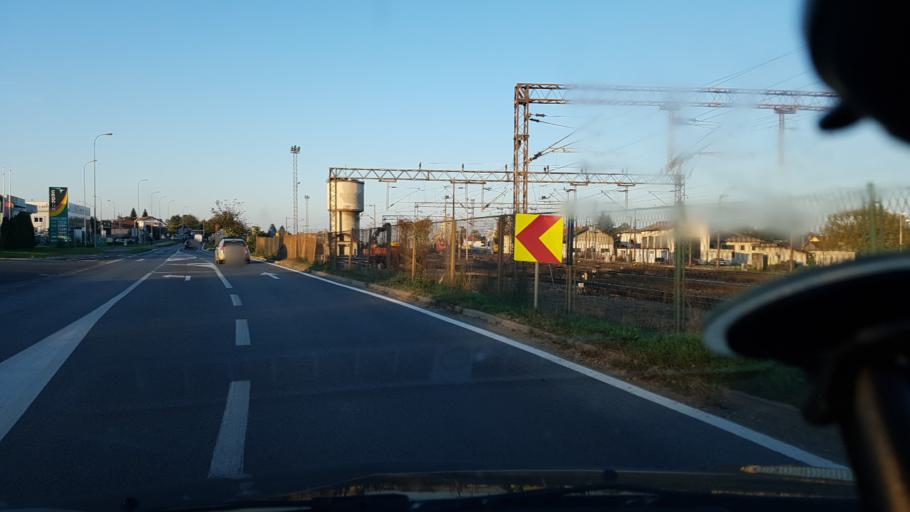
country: HR
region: Koprivnicko-Krizevacka
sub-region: Grad Koprivnica
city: Koprivnica
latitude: 46.1595
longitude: 16.8119
